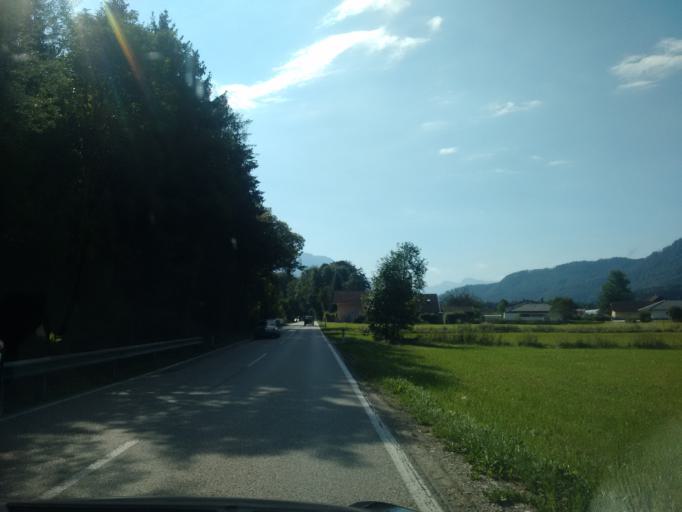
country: AT
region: Upper Austria
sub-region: Politischer Bezirk Gmunden
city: Gruenau im Almtal
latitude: 47.8800
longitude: 13.9404
